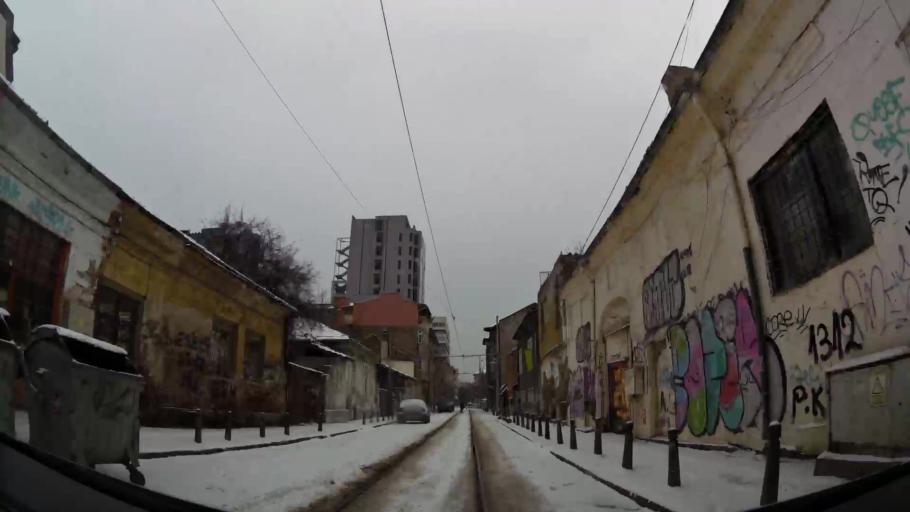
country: BG
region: Sofia-Capital
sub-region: Stolichna Obshtina
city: Sofia
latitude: 42.7007
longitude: 23.3122
